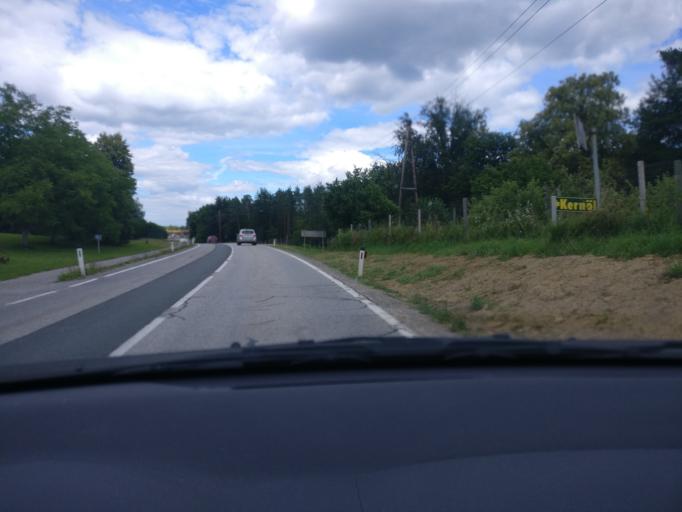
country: AT
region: Styria
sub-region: Politischer Bezirk Weiz
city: Oberrettenbach
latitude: 47.1699
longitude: 15.7834
